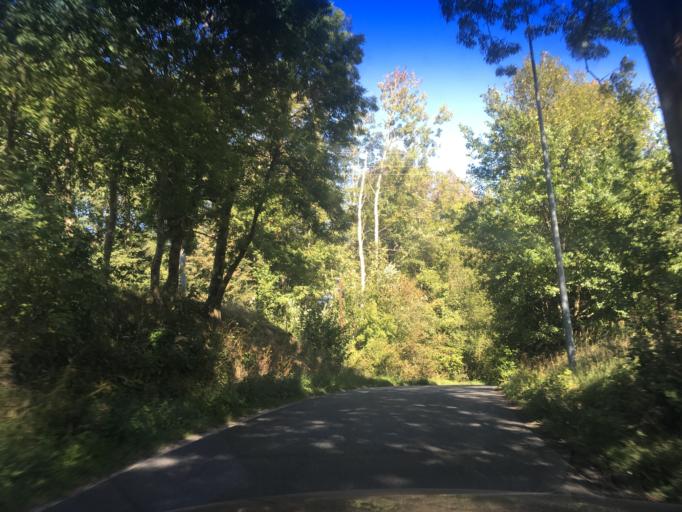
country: PL
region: Lower Silesian Voivodeship
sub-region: Powiat lubanski
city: Lesna
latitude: 51.0311
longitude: 15.2269
